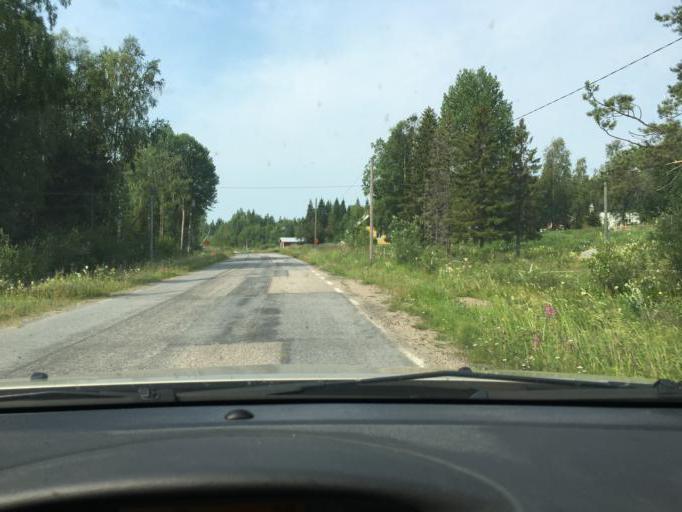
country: SE
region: Norrbotten
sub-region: Kalix Kommun
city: Rolfs
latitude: 65.7741
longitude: 23.0025
